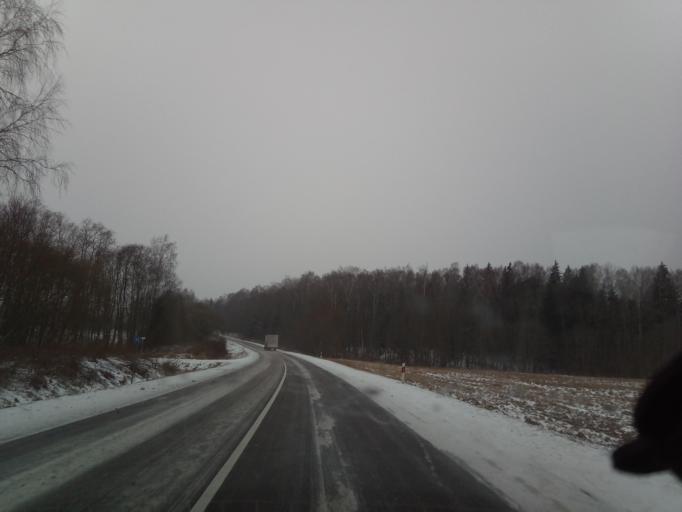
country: LT
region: Utenos apskritis
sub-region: Anyksciai
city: Anyksciai
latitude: 55.4036
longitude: 25.1337
